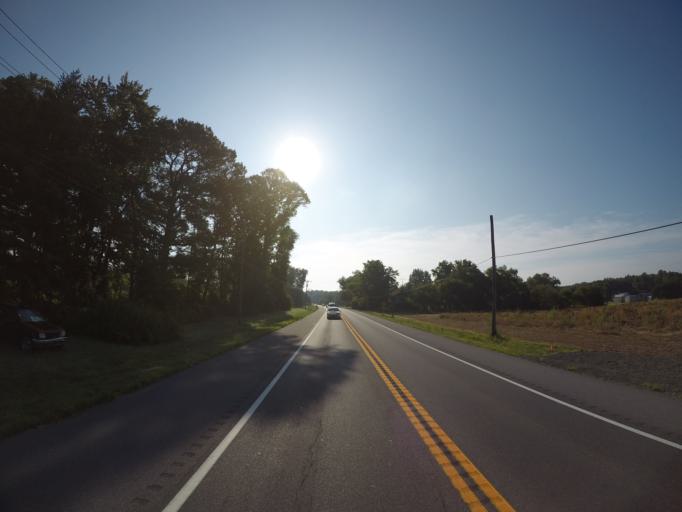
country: US
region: Delaware
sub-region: Sussex County
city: Georgetown
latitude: 38.6983
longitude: -75.4447
